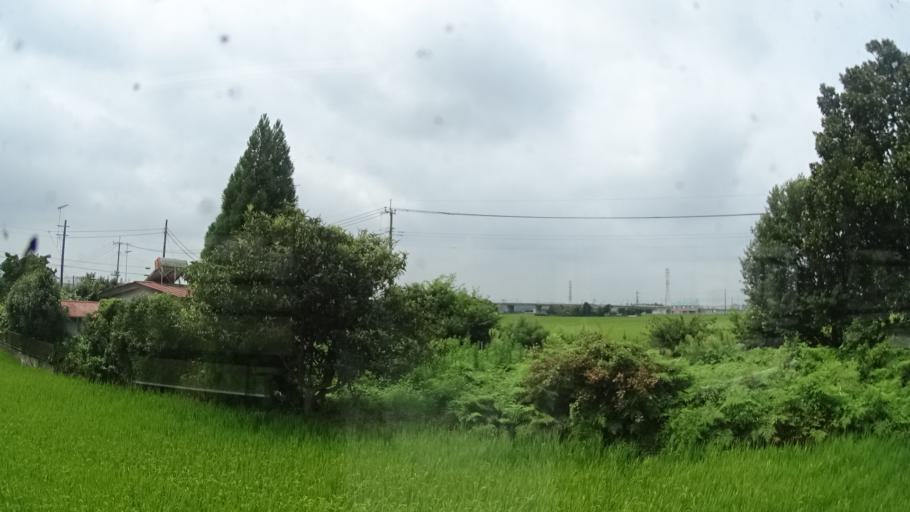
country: JP
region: Ibaraki
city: Shimodate
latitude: 36.3048
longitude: 139.9720
